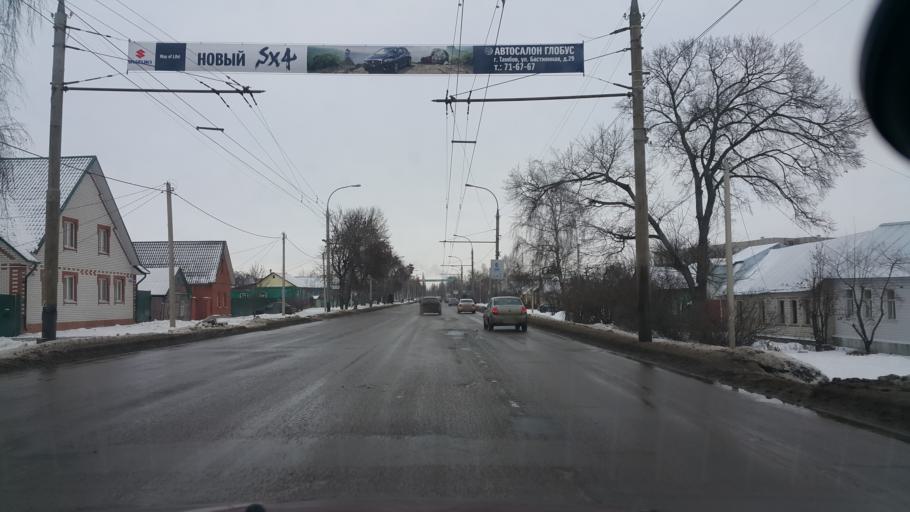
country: RU
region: Tambov
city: Tambov
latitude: 52.7282
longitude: 41.4028
